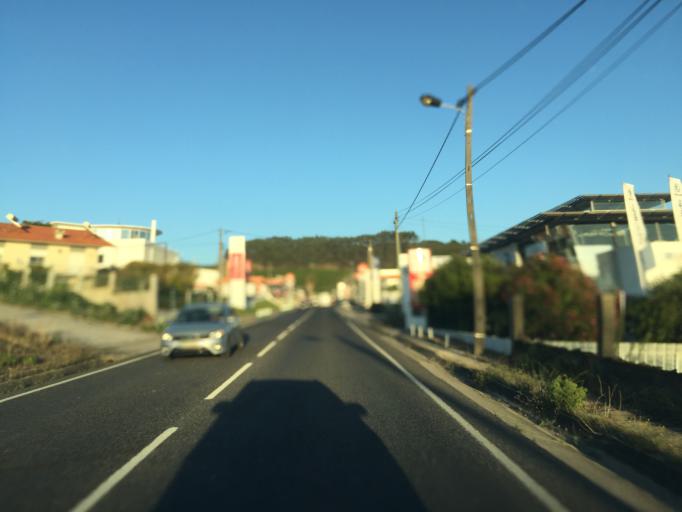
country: PT
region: Lisbon
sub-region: Torres Vedras
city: Torres Vedras
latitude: 39.0709
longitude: -9.2461
